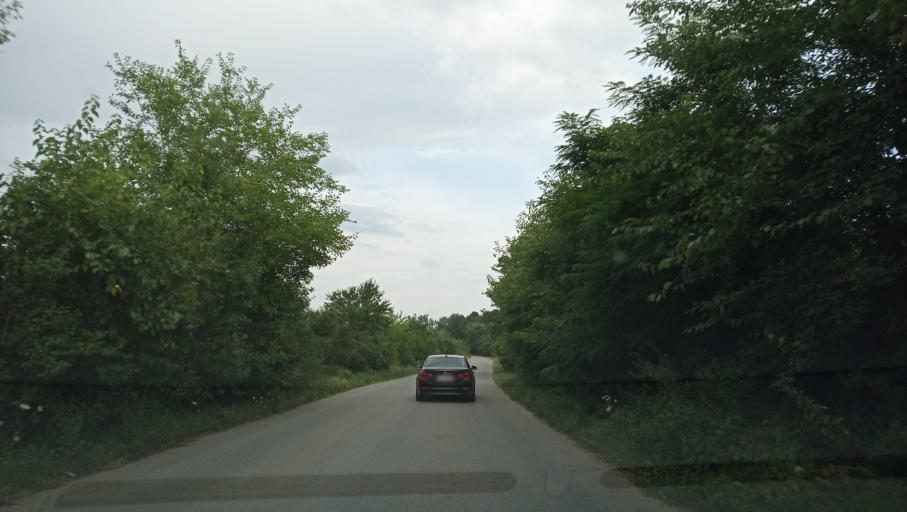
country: RO
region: Giurgiu
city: Iepuresti
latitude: 44.2566
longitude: 25.8930
